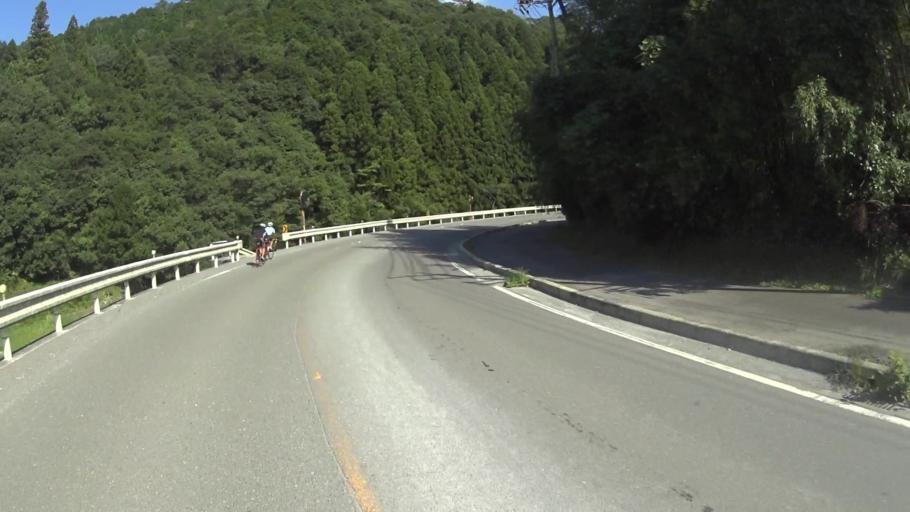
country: JP
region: Kyoto
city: Kameoka
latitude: 34.9298
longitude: 135.5608
